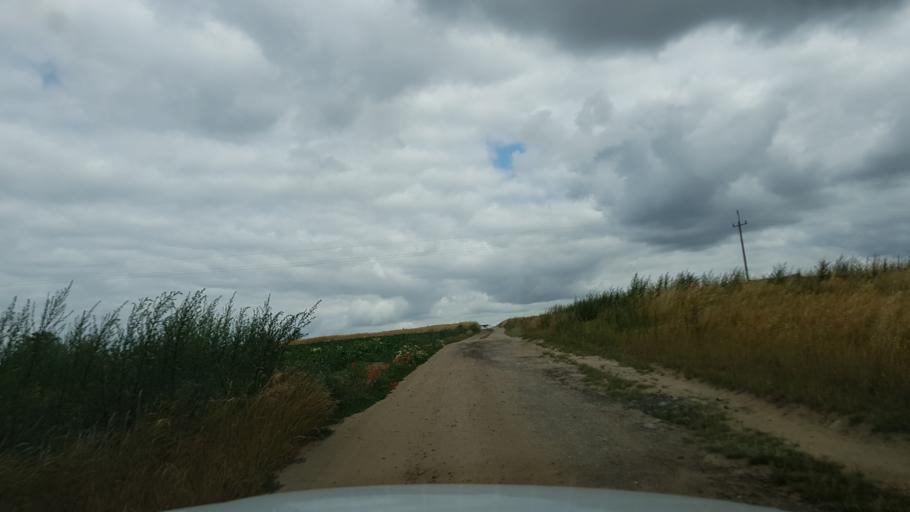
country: PL
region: West Pomeranian Voivodeship
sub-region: Powiat mysliborski
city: Mysliborz
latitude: 52.9309
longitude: 14.8761
